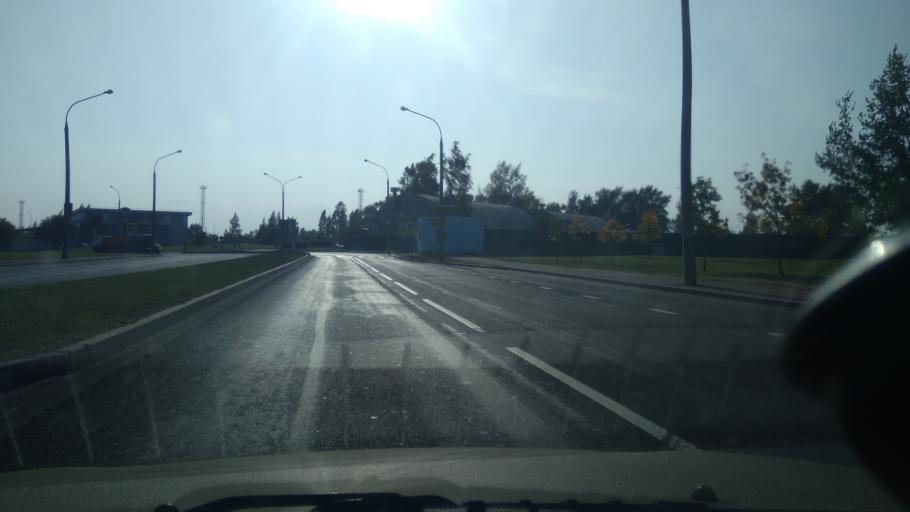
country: BY
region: Minsk
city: Vyaliki Trastsyanets
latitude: 53.8331
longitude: 27.6970
